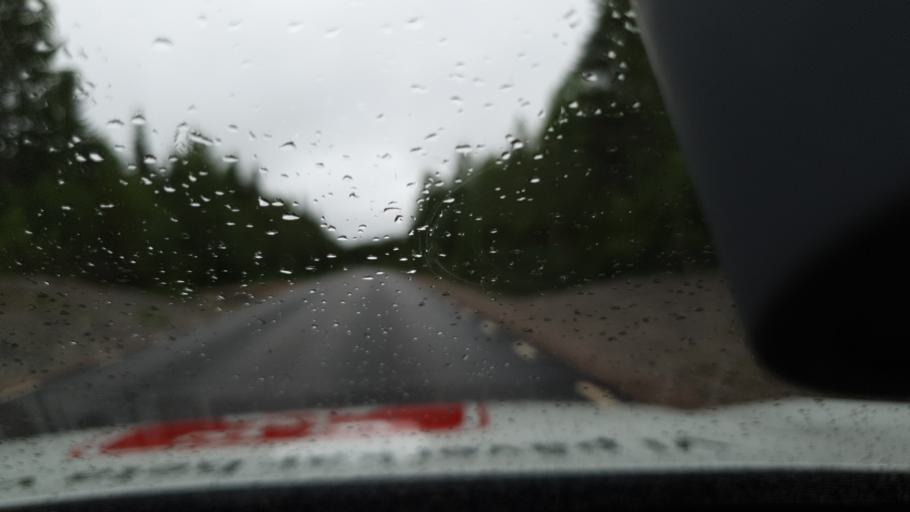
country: SE
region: Norrbotten
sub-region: Overtornea Kommun
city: OEvertornea
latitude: 66.4925
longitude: 23.4426
